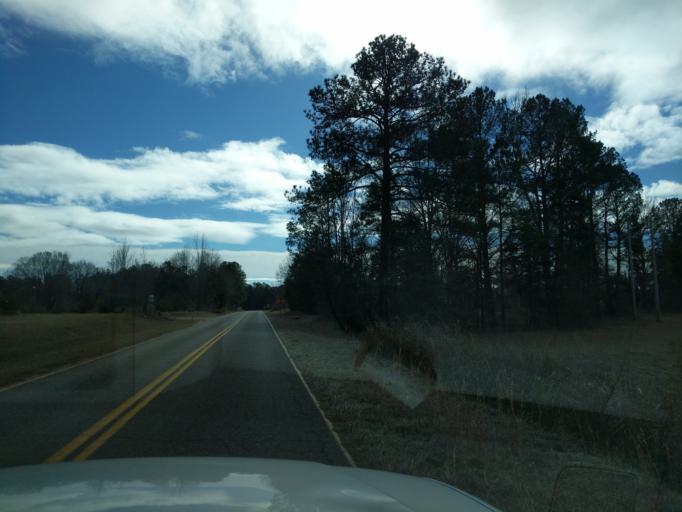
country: US
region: South Carolina
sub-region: Edgefield County
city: Edgefield
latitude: 33.8738
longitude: -81.9964
